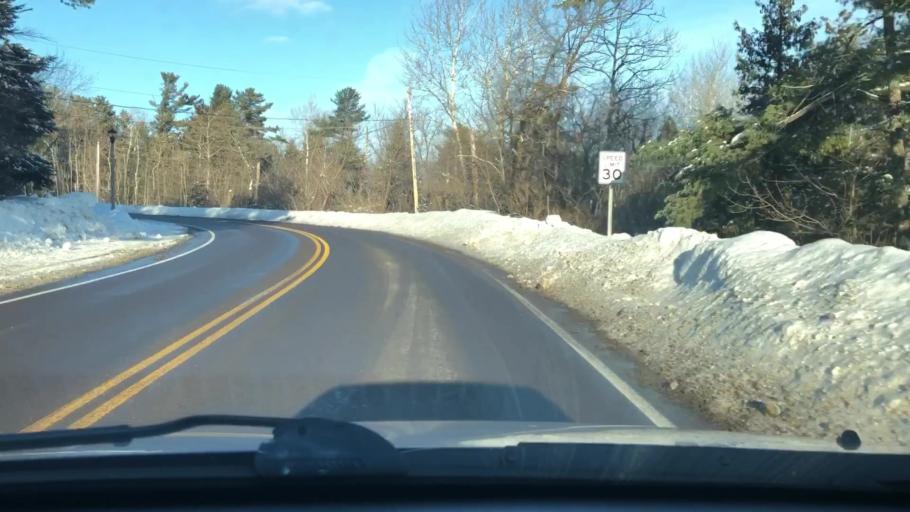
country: US
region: Minnesota
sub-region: Saint Louis County
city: Duluth
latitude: 46.8198
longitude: -92.0699
